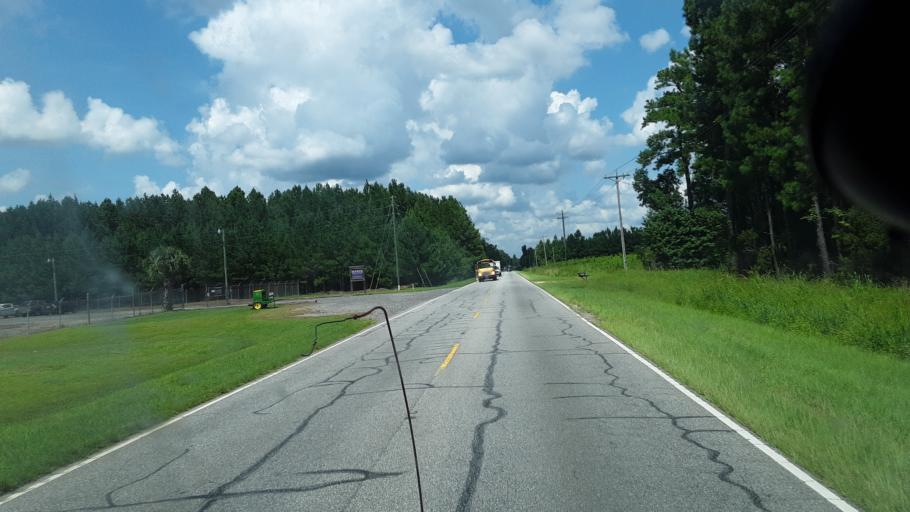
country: US
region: South Carolina
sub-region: Williamsburg County
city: Andrews
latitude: 33.6086
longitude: -79.4381
